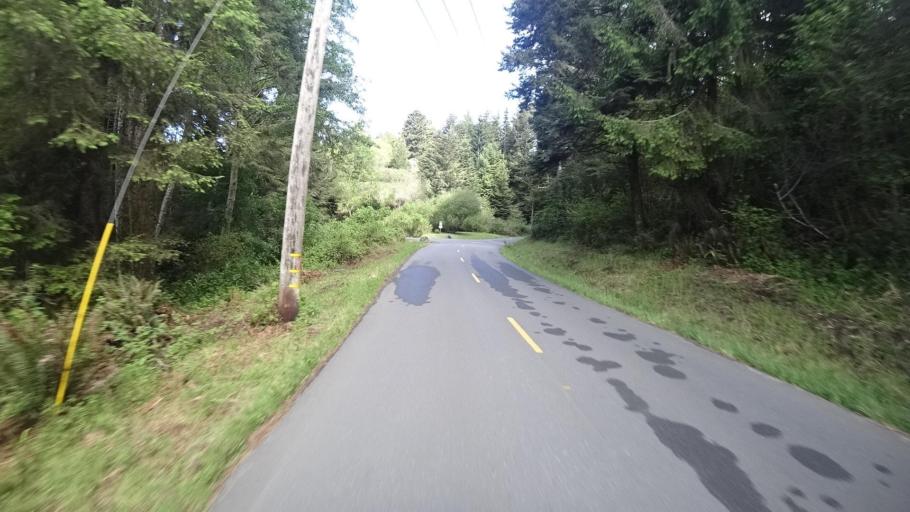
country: US
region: California
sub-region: Humboldt County
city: McKinleyville
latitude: 40.9193
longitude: -124.0791
